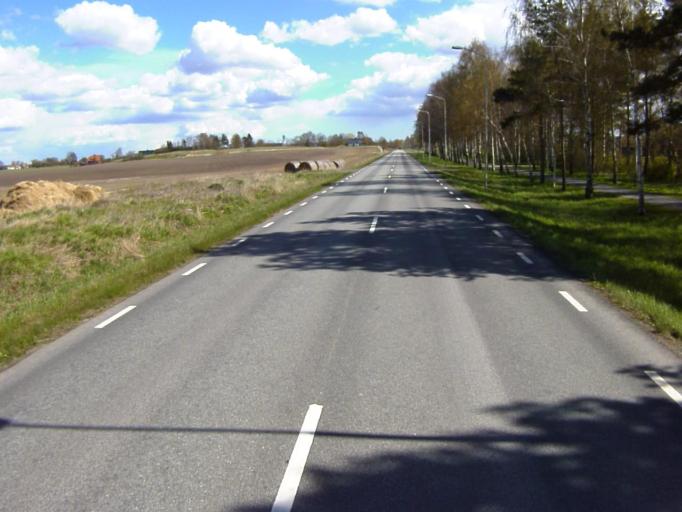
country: SE
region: Skane
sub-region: Kristianstads Kommun
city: Kristianstad
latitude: 56.0165
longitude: 14.0954
